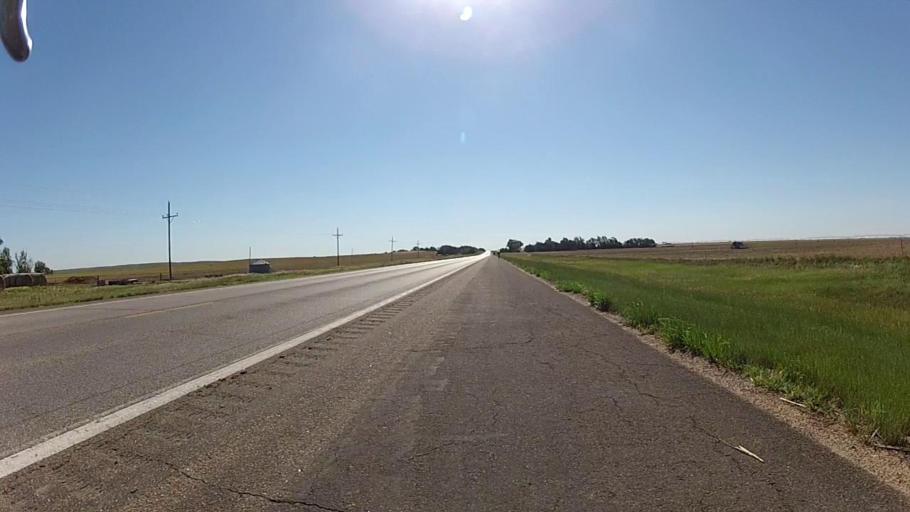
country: US
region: Kansas
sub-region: Kiowa County
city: Greensburg
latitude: 37.5862
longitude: -99.5911
